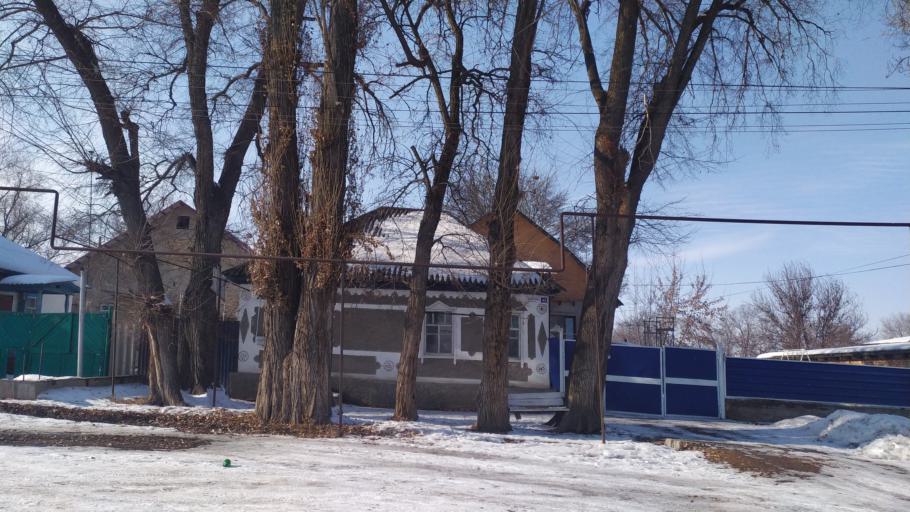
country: KZ
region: Almaty Oblysy
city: Burunday
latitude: 43.2463
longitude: 76.4332
